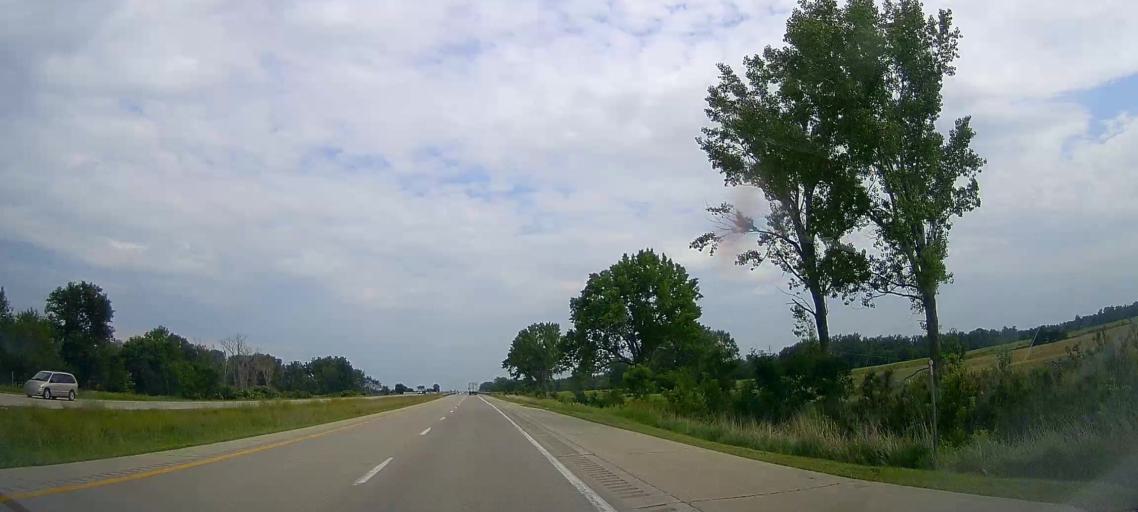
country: US
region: Nebraska
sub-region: Burt County
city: Tekamah
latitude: 41.8230
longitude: -96.0748
